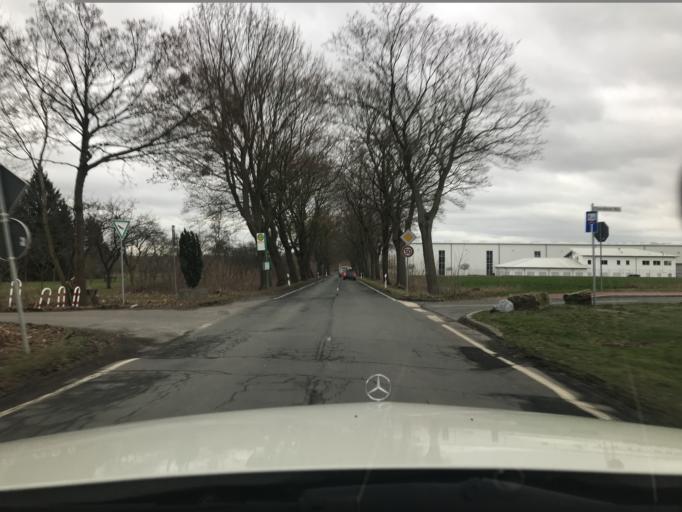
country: DE
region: North Rhine-Westphalia
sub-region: Regierungsbezirk Arnsberg
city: Hamm
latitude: 51.6210
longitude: 7.8667
